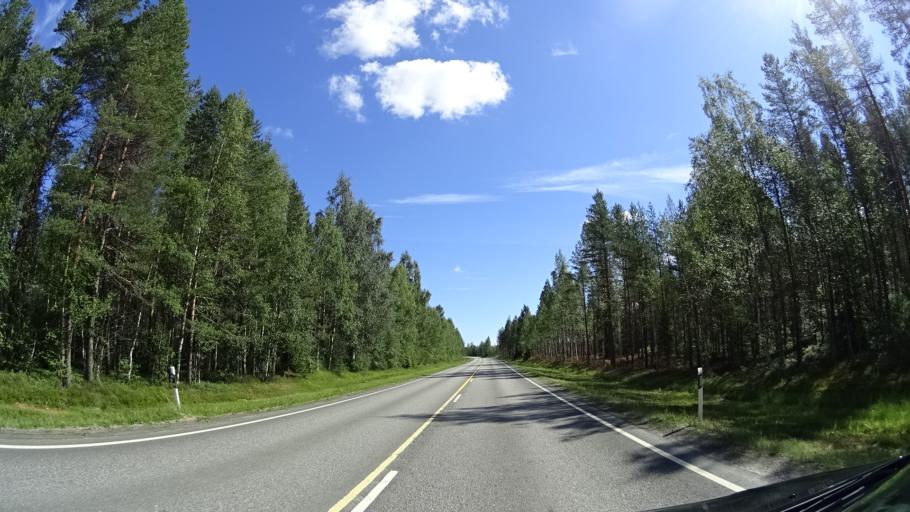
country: FI
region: Pirkanmaa
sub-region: Luoteis-Pirkanmaa
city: Kihnioe
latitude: 62.2190
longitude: 23.2687
